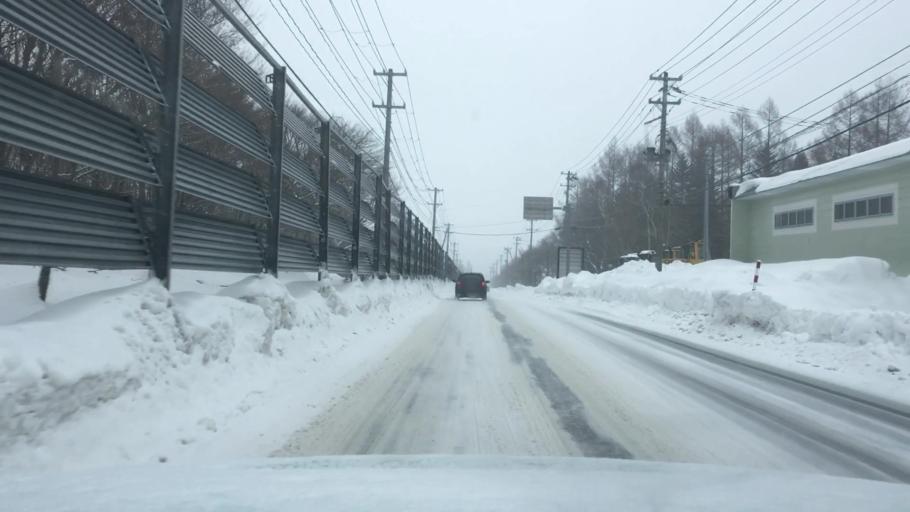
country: JP
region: Akita
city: Hanawa
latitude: 40.0090
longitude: 140.9767
